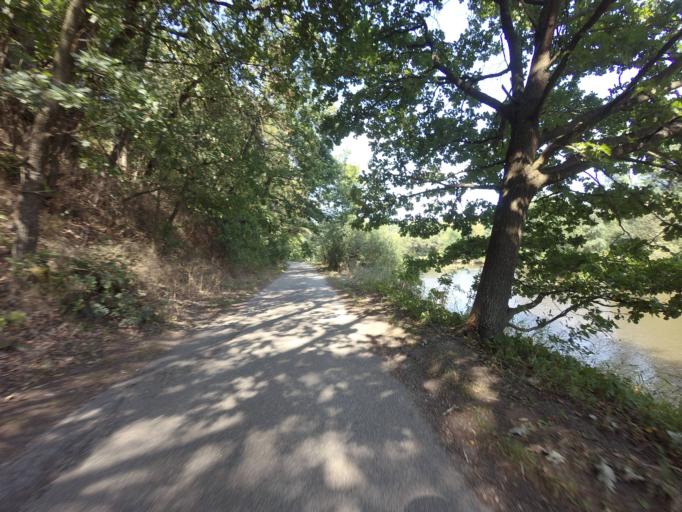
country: CZ
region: Jihocesky
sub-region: Okres Ceske Budejovice
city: Hluboka nad Vltavou
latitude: 49.0598
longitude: 14.4428
